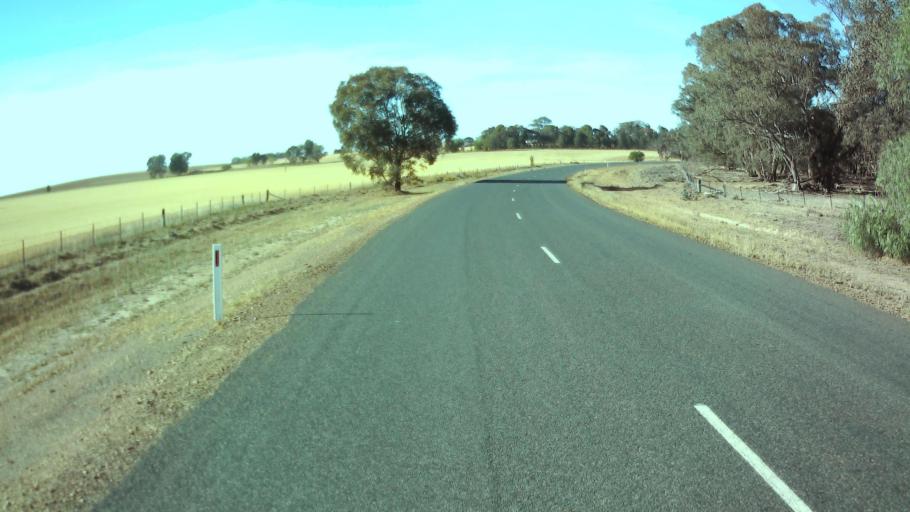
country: AU
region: New South Wales
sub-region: Weddin
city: Grenfell
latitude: -33.9857
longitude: 148.1409
